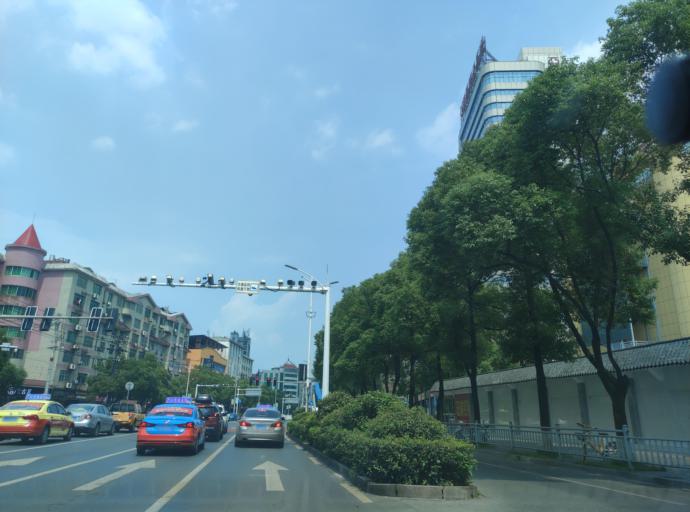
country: CN
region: Jiangxi Sheng
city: Pingxiang
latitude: 27.6426
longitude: 113.8625
